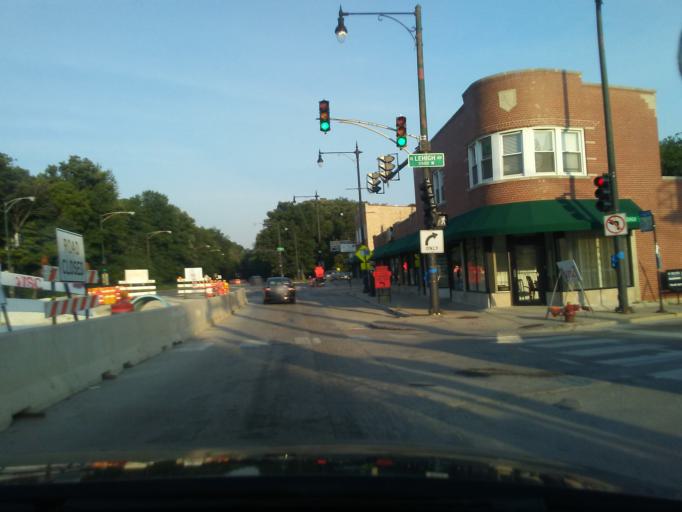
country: US
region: Illinois
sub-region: Cook County
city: Lincolnwood
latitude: 41.9974
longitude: -87.7659
